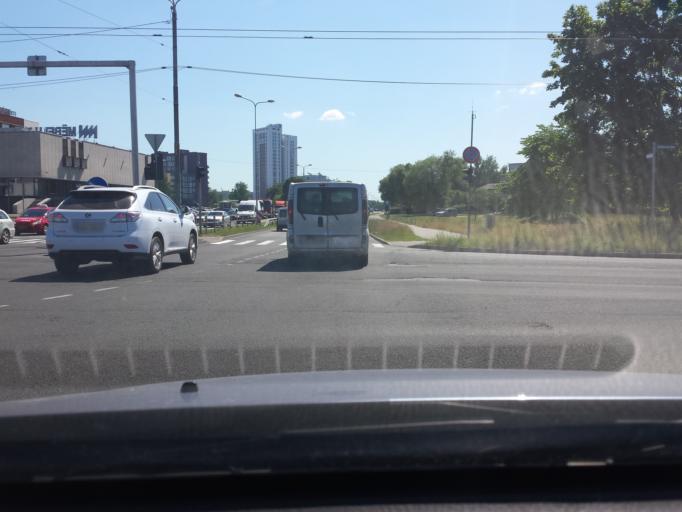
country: LV
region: Riga
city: Jaunciems
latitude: 56.9568
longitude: 24.1894
